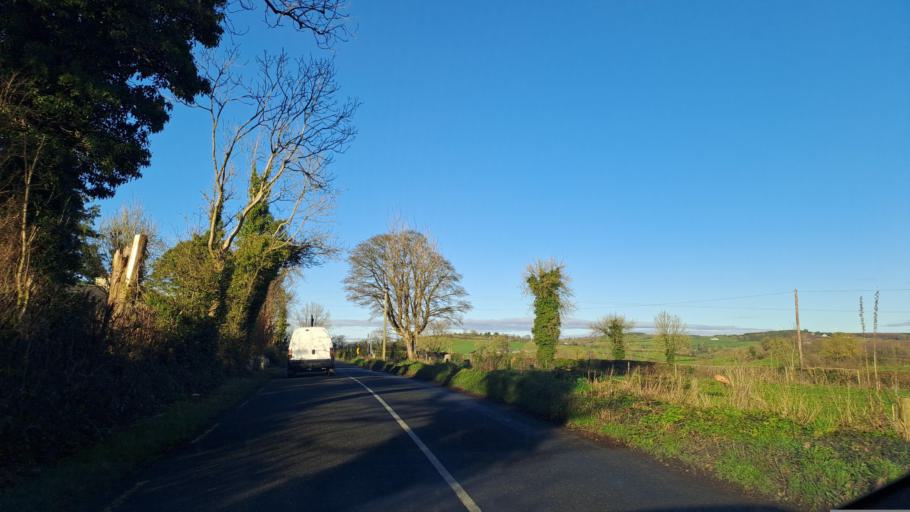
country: IE
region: Ulster
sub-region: An Cabhan
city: Mullagh
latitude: 53.8376
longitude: -6.9538
